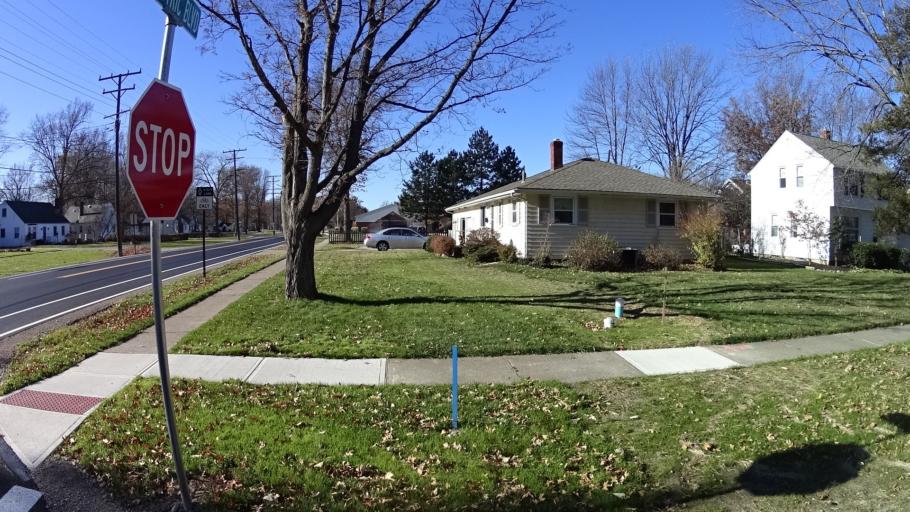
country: US
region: Ohio
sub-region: Lorain County
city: Avon Lake
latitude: 41.5098
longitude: -82.0245
